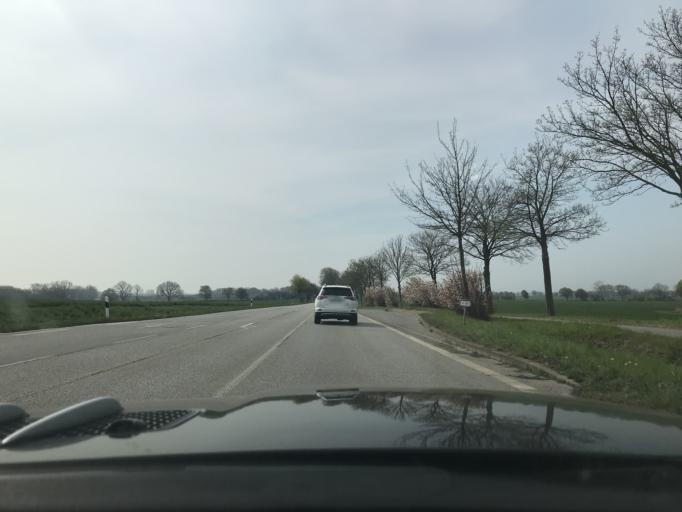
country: DE
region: Schleswig-Holstein
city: Grube
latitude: 54.2651
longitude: 11.0337
